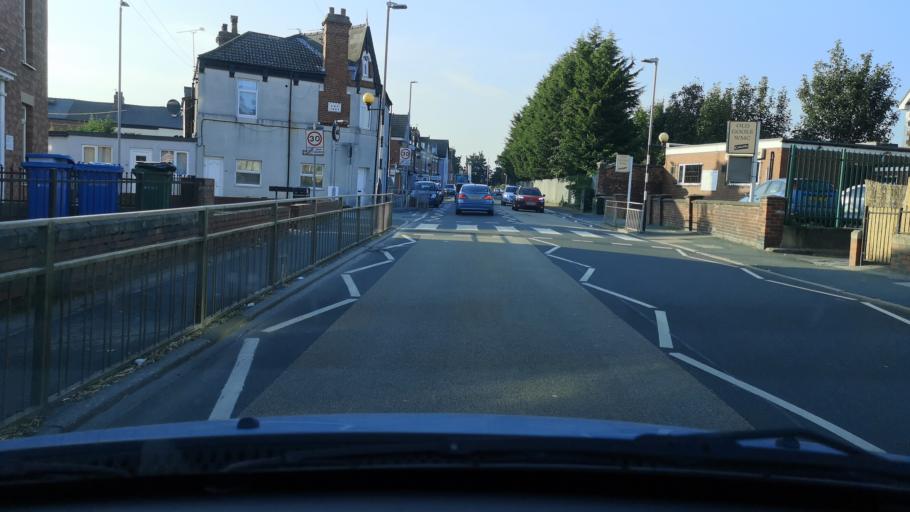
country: GB
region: England
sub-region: East Riding of Yorkshire
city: Goole
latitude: 53.6936
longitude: -0.8675
